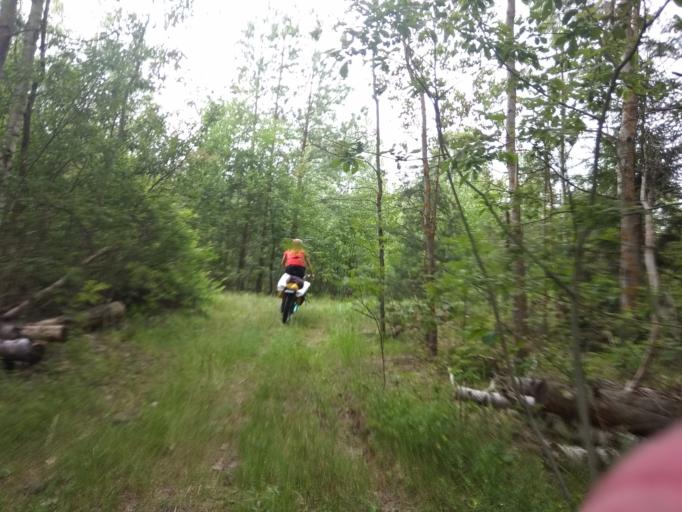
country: RU
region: Moskovskaya
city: Misheronskiy
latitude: 55.6505
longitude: 39.6912
